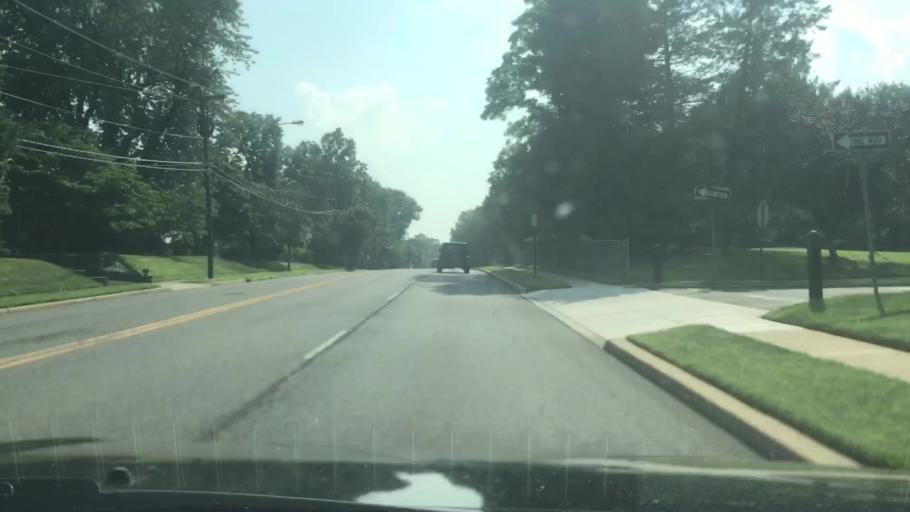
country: US
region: New Jersey
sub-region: Monmouth County
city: Eatontown
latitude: 40.3010
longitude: -74.0462
